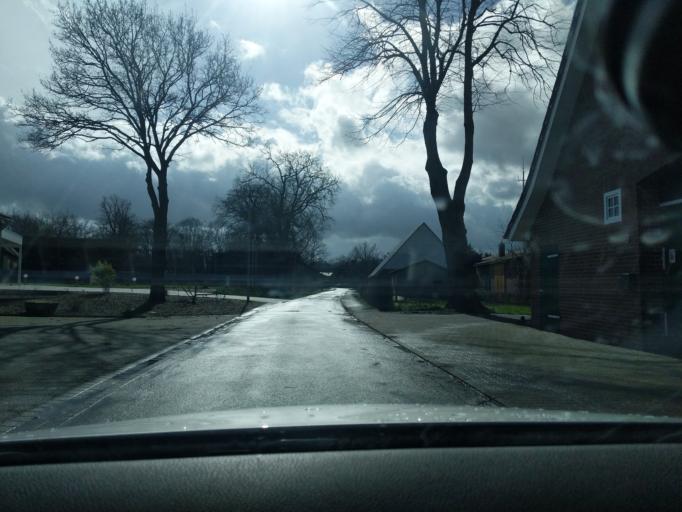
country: DE
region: Lower Saxony
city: Kranenburg
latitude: 53.6081
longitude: 9.2075
